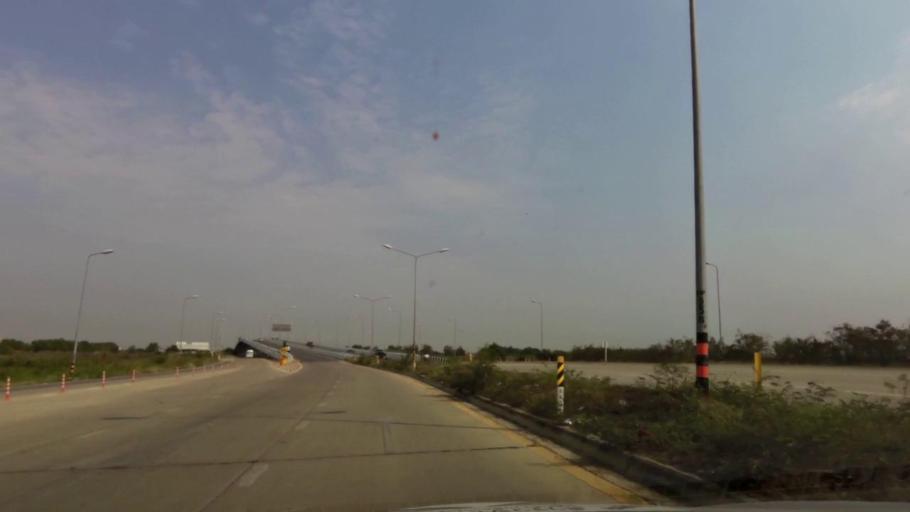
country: TH
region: Phra Nakhon Si Ayutthaya
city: Phra Nakhon Si Ayutthaya
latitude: 14.3303
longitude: 100.5797
